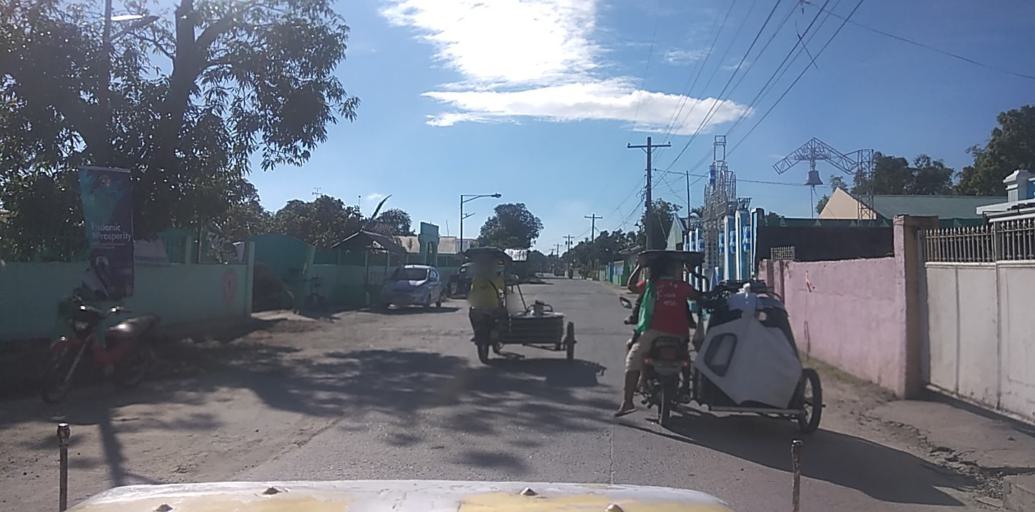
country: PH
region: Central Luzon
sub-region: Province of Pampanga
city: San Patricio
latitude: 15.1097
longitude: 120.7121
